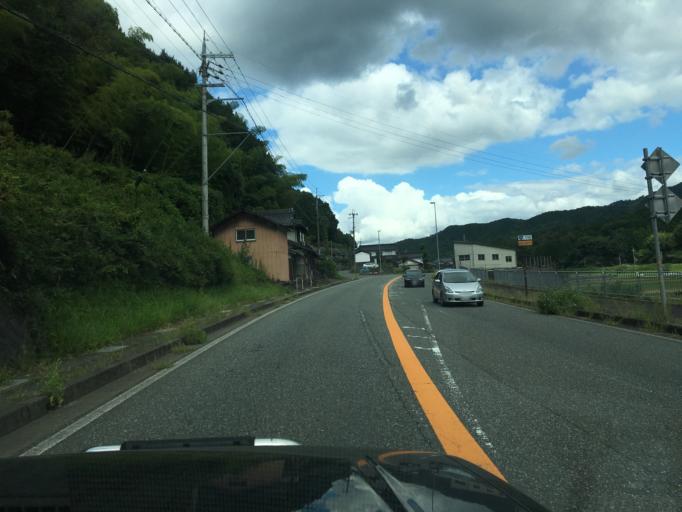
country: JP
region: Kyoto
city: Fukuchiyama
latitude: 35.3224
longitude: 134.8977
